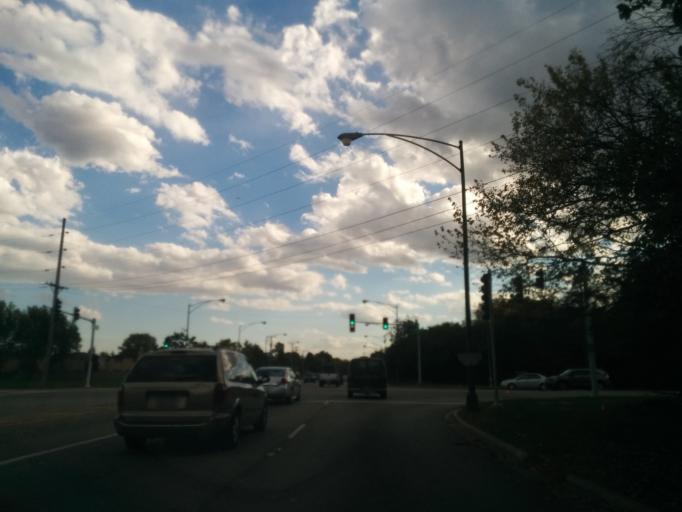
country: US
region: Illinois
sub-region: Cook County
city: Norridge
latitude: 41.9670
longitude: -87.8467
